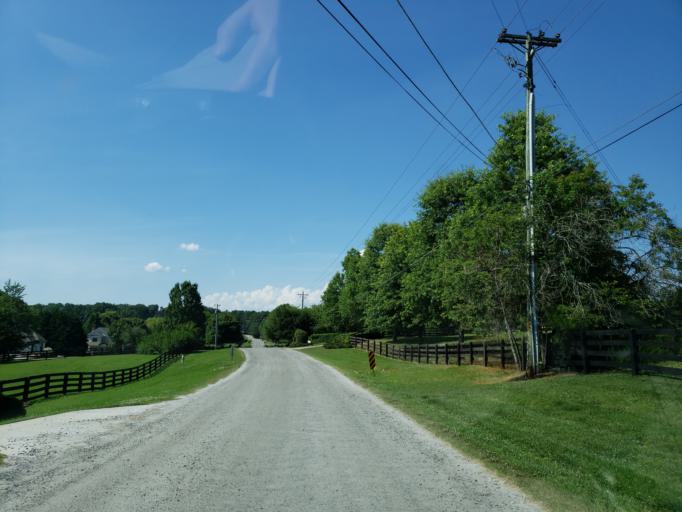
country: US
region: Georgia
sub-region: Fulton County
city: Milton
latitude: 34.1185
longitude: -84.3109
